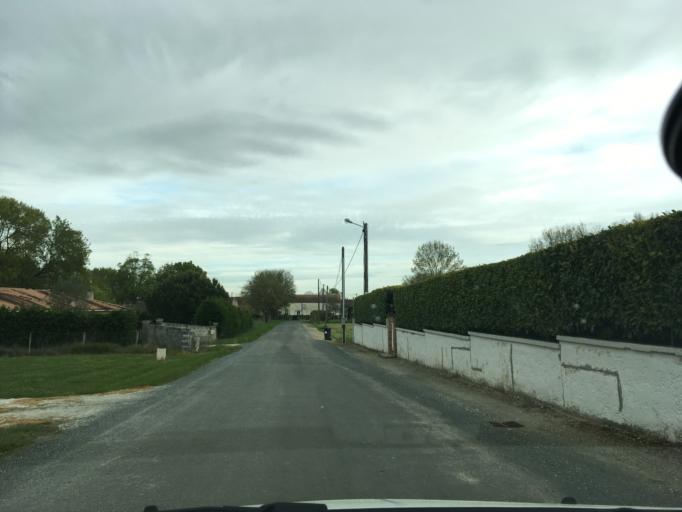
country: FR
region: Aquitaine
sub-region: Departement de la Gironde
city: Lesparre-Medoc
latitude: 45.3103
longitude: -0.8936
